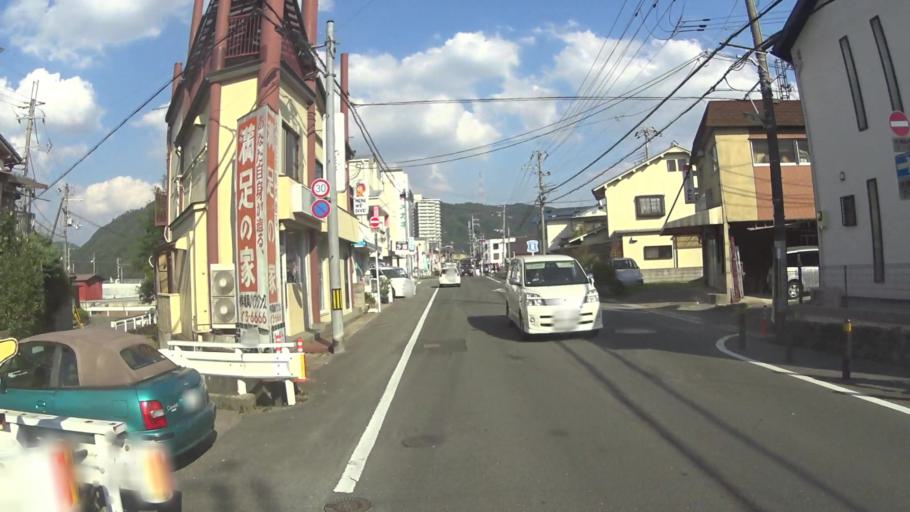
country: JP
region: Kyoto
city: Kameoka
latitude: 35.0095
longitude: 135.5984
